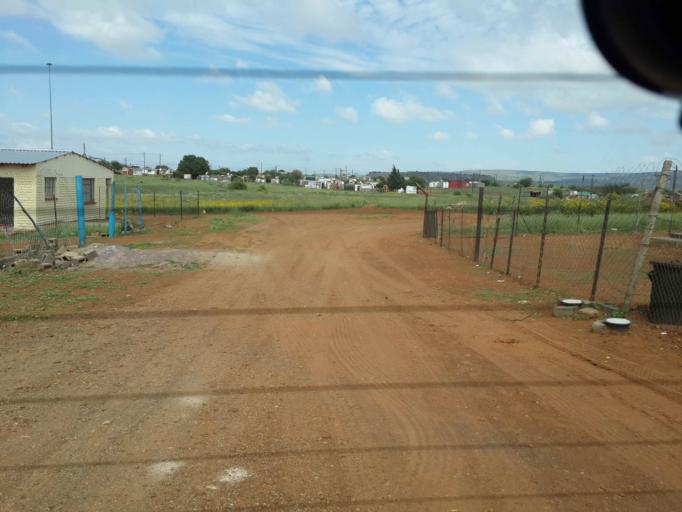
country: ZA
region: Northern Cape
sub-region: Siyanda District Municipality
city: Danielskuil
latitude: -28.1971
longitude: 23.5537
